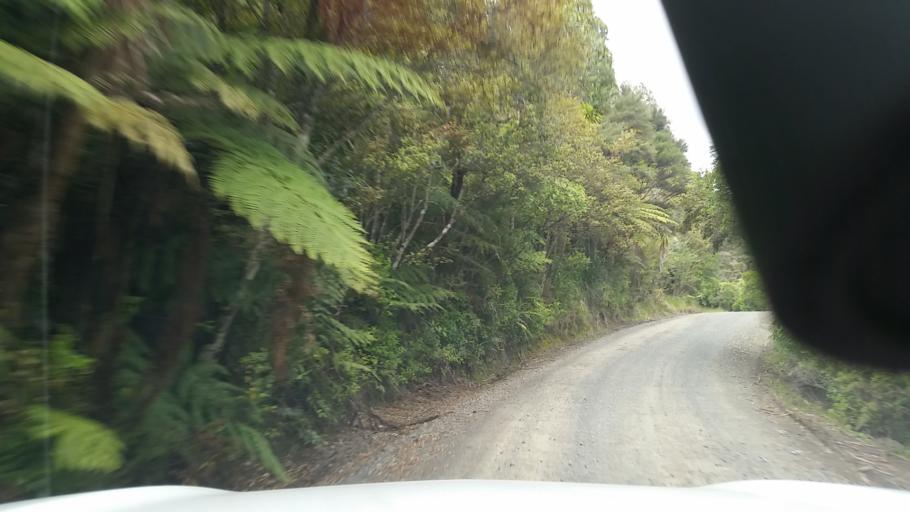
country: NZ
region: Auckland
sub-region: Auckland
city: Muriwai Beach
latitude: -36.8741
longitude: 174.5085
